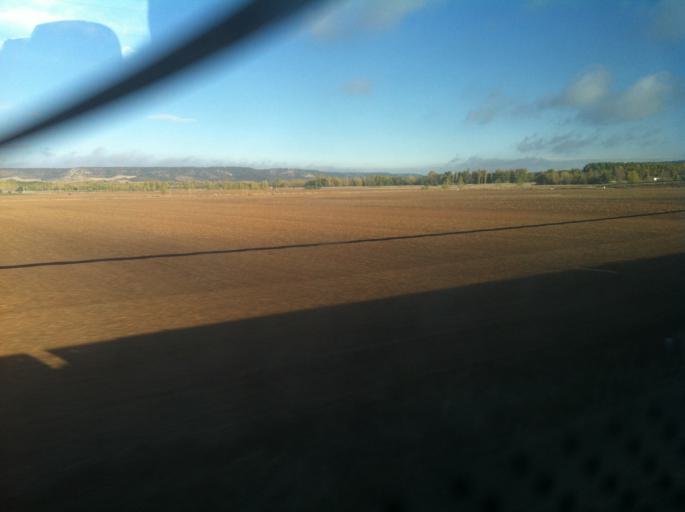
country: ES
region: Castille and Leon
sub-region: Provincia de Palencia
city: Hornillos de Cerrato
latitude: 42.0327
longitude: -4.2728
